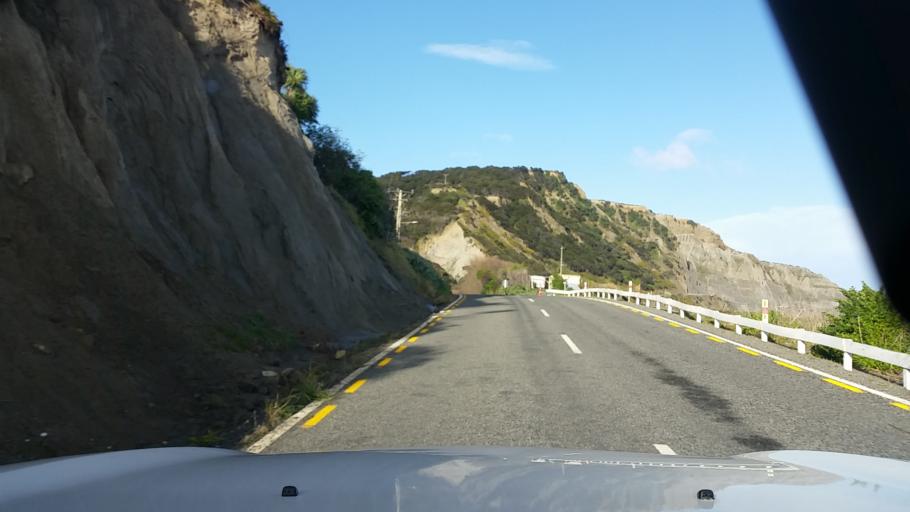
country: NZ
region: Wellington
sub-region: South Wairarapa District
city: Waipawa
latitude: -41.4593
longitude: 175.2197
